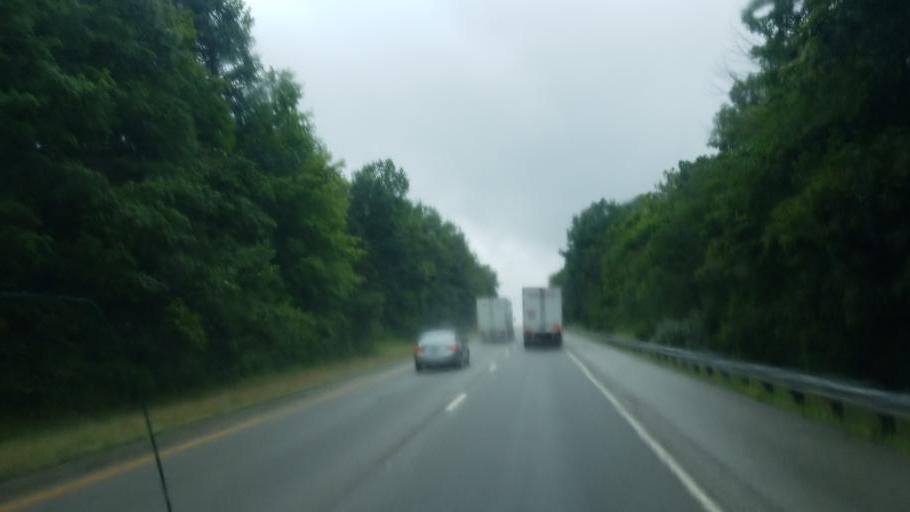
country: US
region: Indiana
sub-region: Putnam County
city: Cloverdale
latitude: 39.5398
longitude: -86.7584
